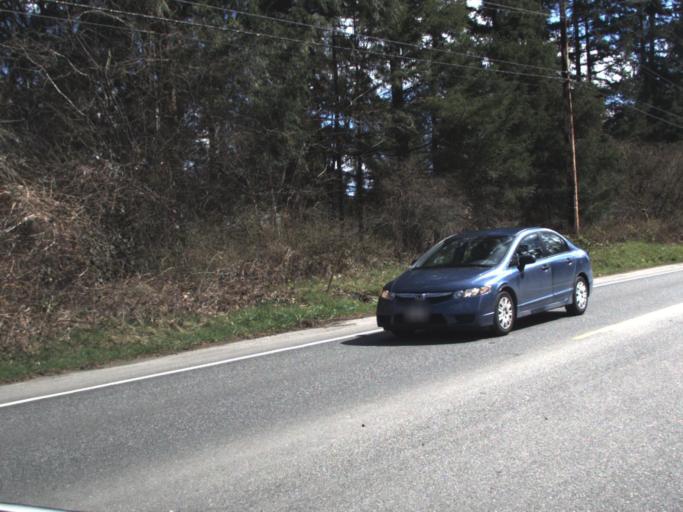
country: US
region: Washington
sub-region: King County
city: Maple Valley
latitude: 47.3780
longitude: -122.0272
